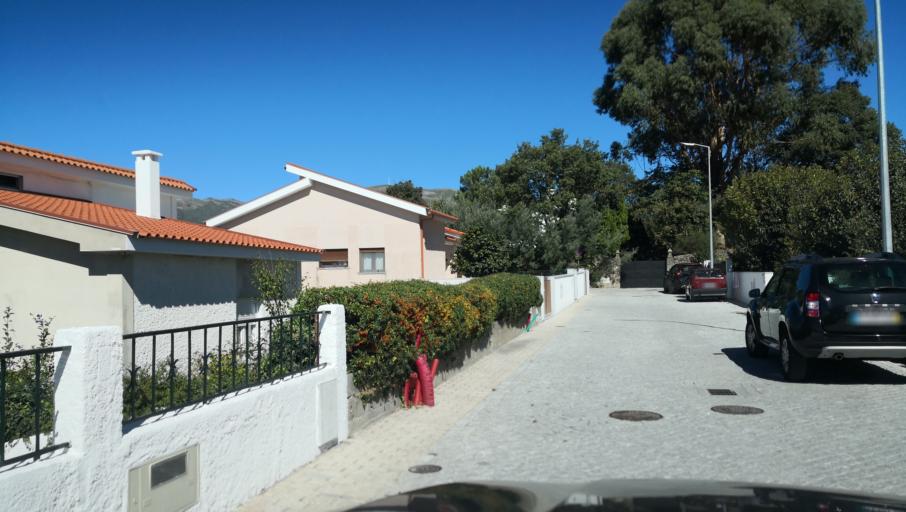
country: PT
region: Vila Real
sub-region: Vila Real
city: Vila Real
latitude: 41.3019
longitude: -7.7501
